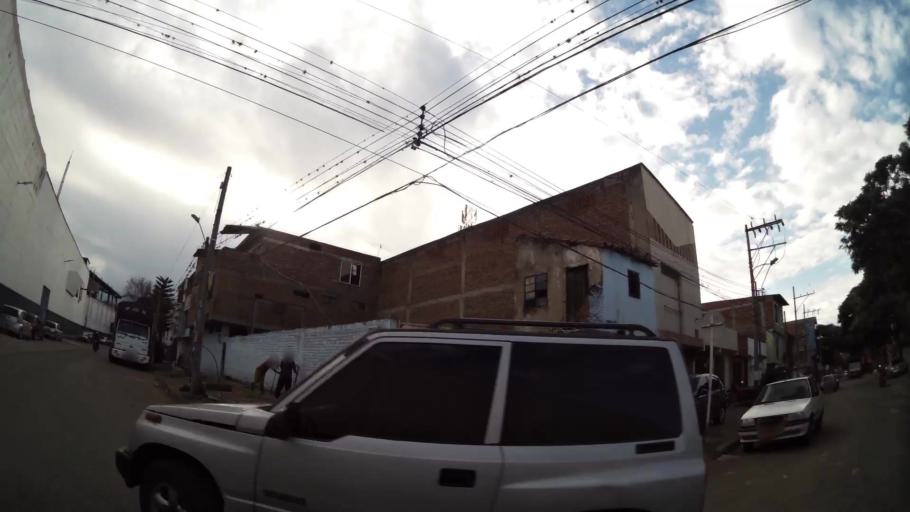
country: CO
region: Valle del Cauca
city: Cali
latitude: 3.4628
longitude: -76.5114
